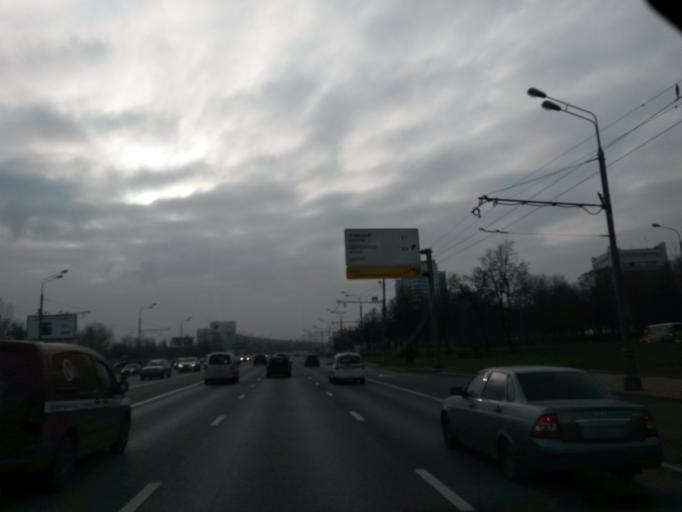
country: RU
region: Moscow
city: Nagornyy
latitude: 55.6360
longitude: 37.6198
